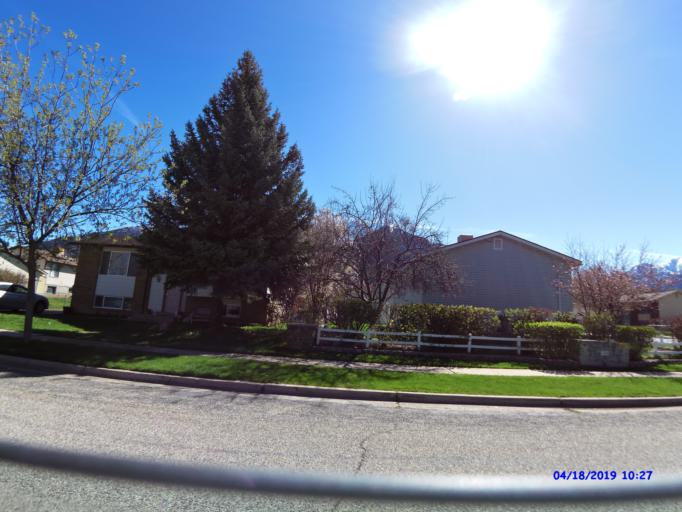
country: US
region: Utah
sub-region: Weber County
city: Harrisville
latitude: 41.2702
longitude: -111.9664
